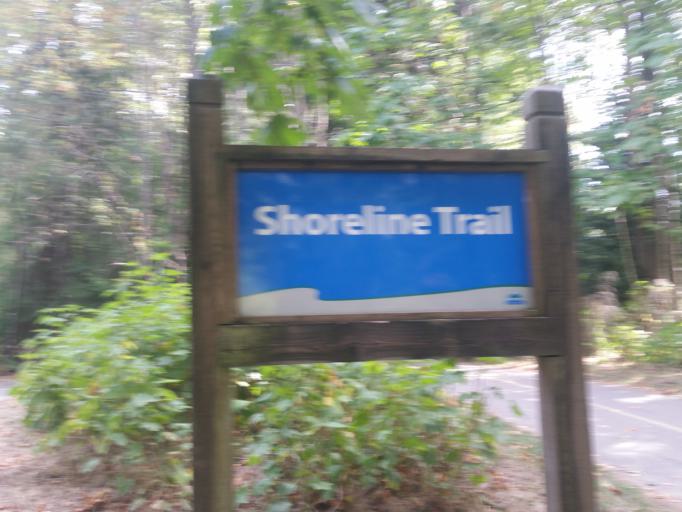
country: CA
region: British Columbia
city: Port Moody
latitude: 49.2798
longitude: -122.8451
